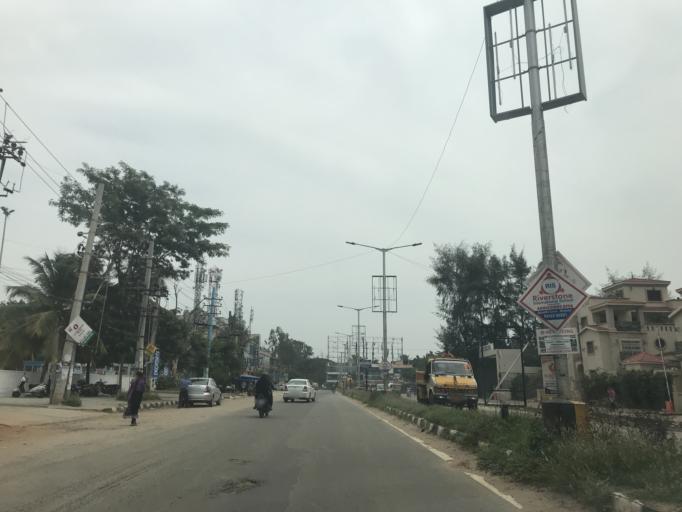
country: IN
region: Karnataka
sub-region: Bangalore Urban
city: Yelahanka
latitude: 13.0663
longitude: 77.6518
